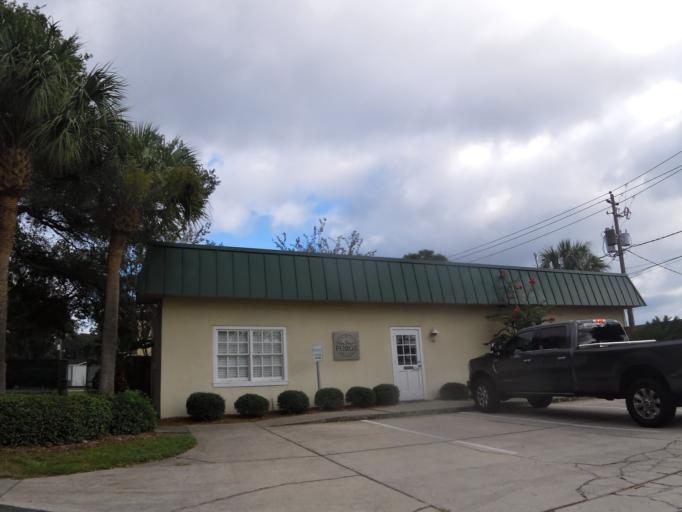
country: US
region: Georgia
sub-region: Glynn County
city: Saint Simons Island
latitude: 31.1598
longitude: -81.3876
